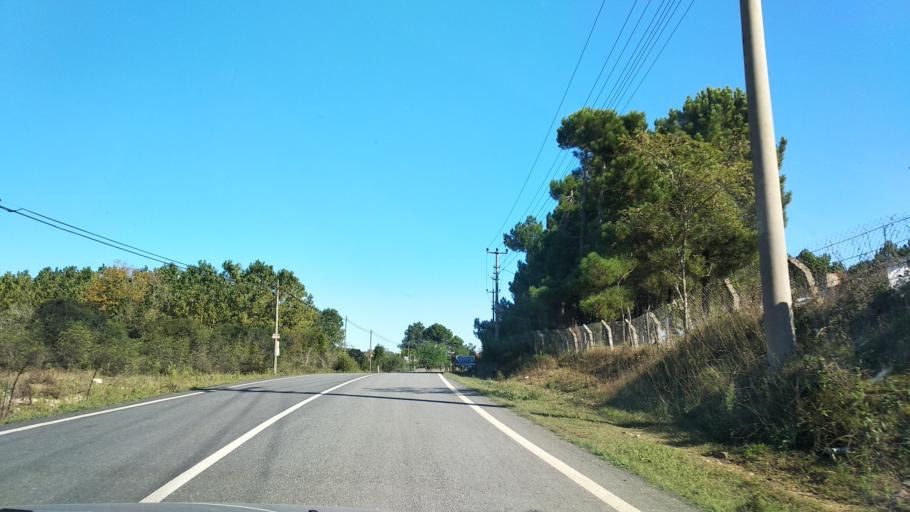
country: TR
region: Sakarya
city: Karasu
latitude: 41.1186
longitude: 30.6147
